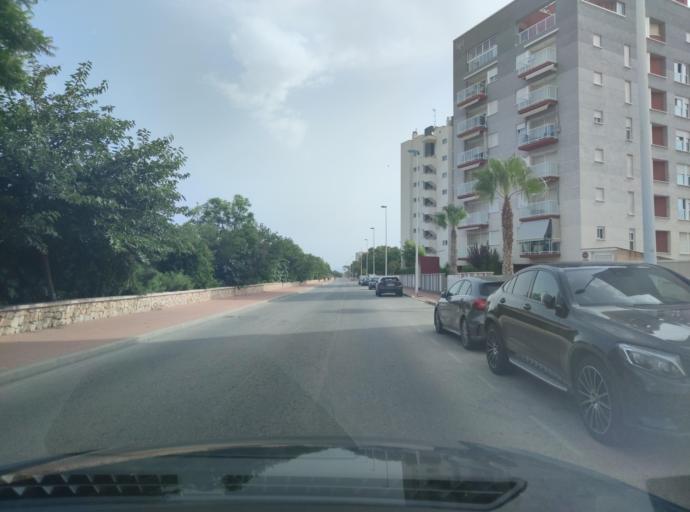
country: ES
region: Valencia
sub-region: Provincia de Alicante
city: Guardamar del Segura
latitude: 38.1034
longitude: -0.6557
